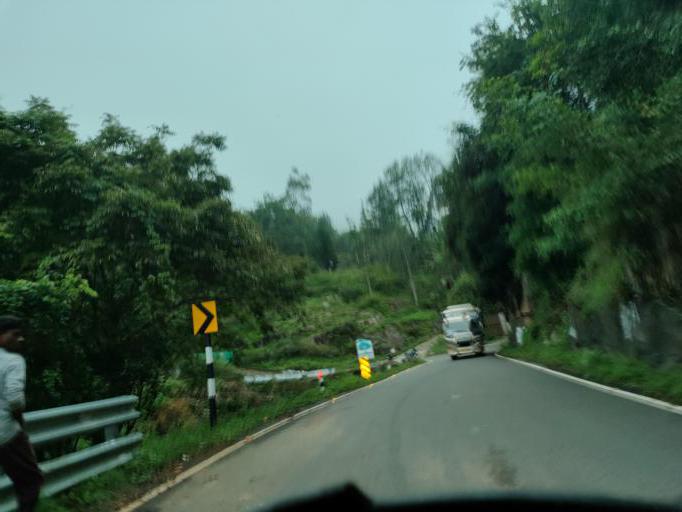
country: IN
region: Tamil Nadu
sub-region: Dindigul
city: Ayakudi
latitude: 10.3566
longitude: 77.5574
